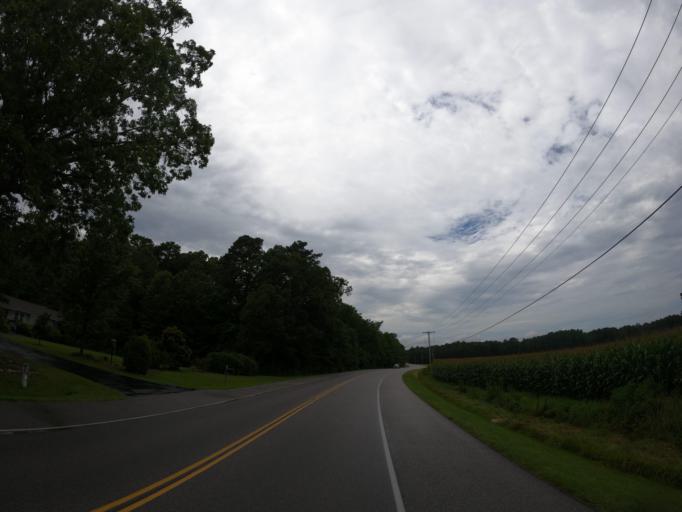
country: US
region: Maryland
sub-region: Saint Mary's County
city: California
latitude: 38.2769
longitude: -76.5455
